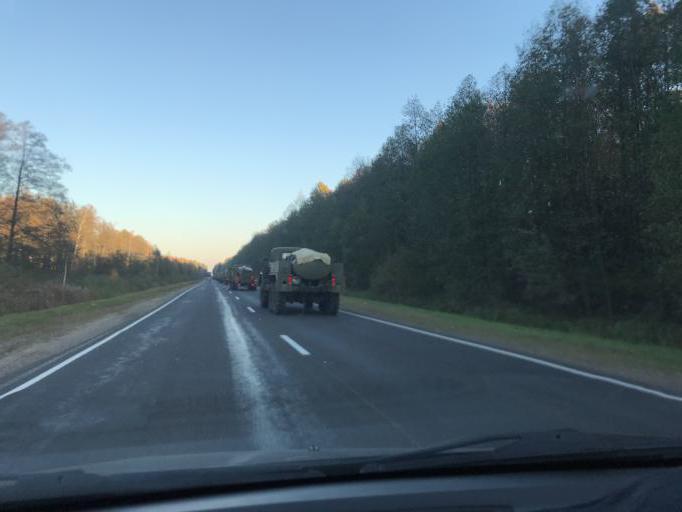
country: BY
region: Minsk
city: Staryya Darohi
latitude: 53.0422
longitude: 28.1527
